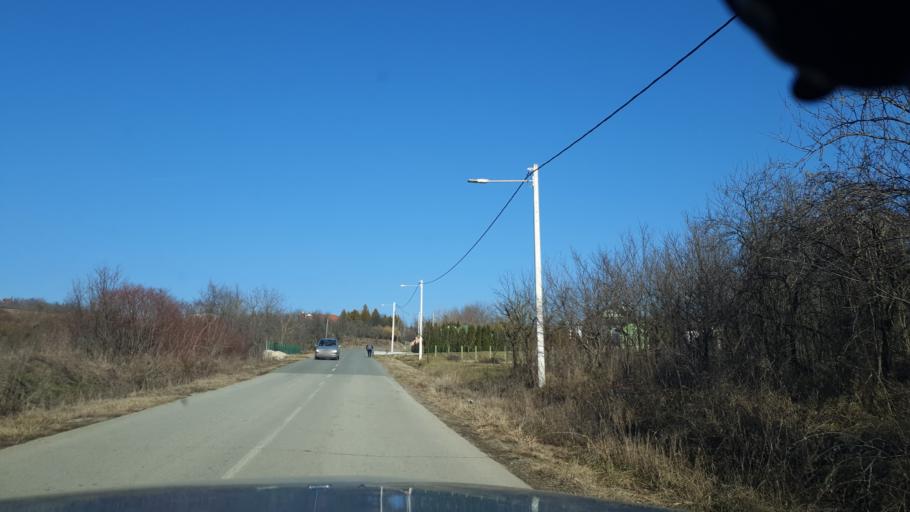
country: RS
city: Vrdnik
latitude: 45.1107
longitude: 19.7669
